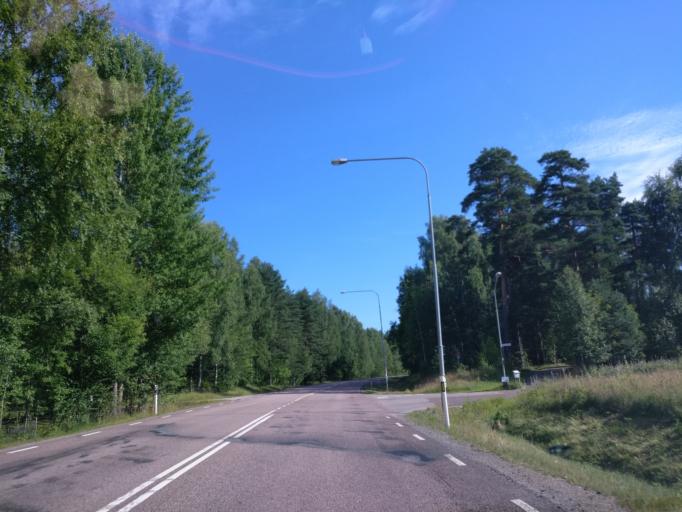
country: SE
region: Vaermland
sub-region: Hagfors Kommun
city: Hagfors
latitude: 60.0551
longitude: 13.7054
